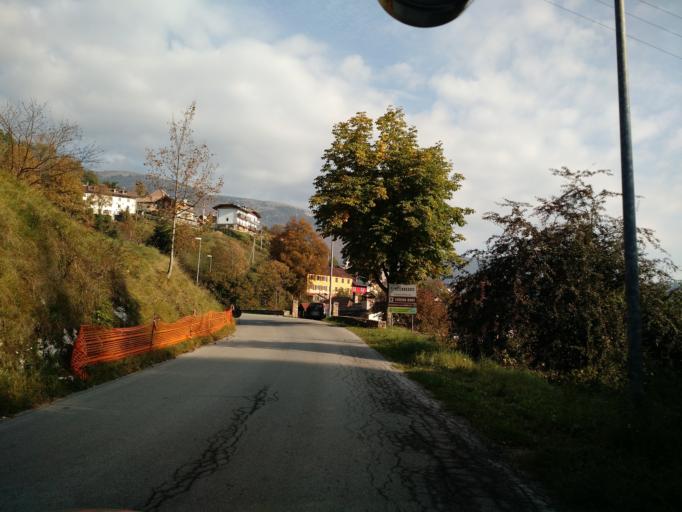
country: IT
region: Veneto
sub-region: Provincia di Vicenza
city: Foza
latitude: 45.8743
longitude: 11.6113
